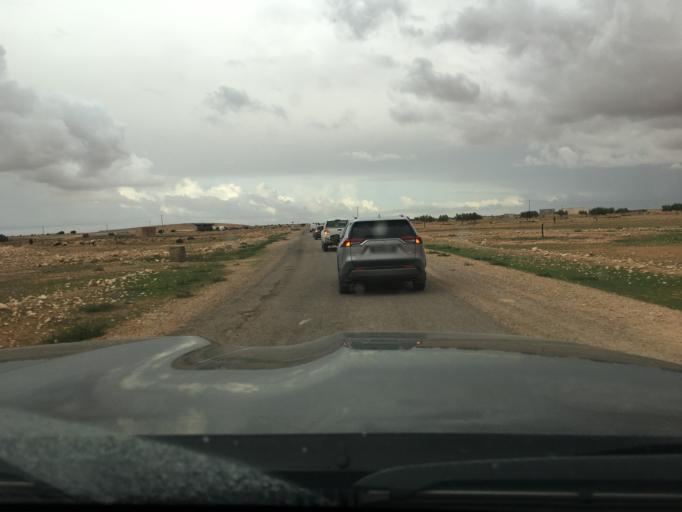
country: TN
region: Madanin
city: Medenine
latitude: 33.2938
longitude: 10.6086
